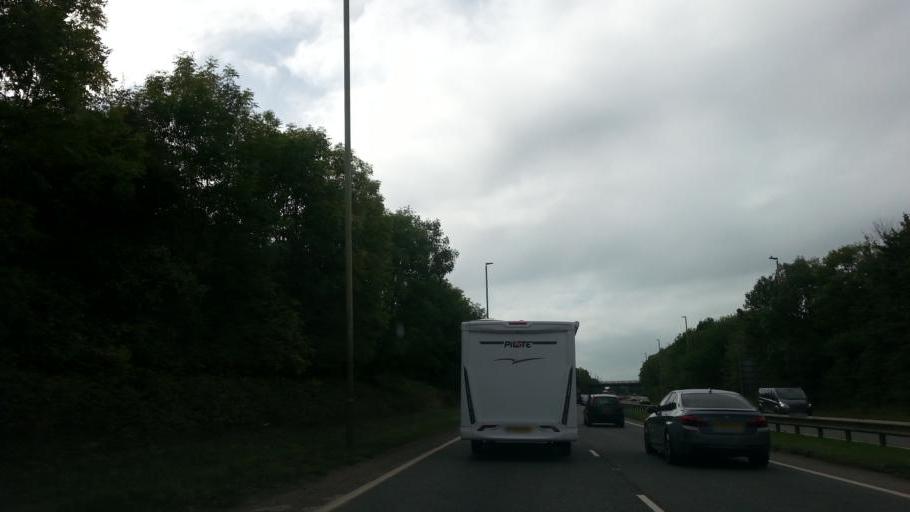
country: GB
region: England
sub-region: Gloucestershire
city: Stonehouse
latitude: 51.8131
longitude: -2.2817
